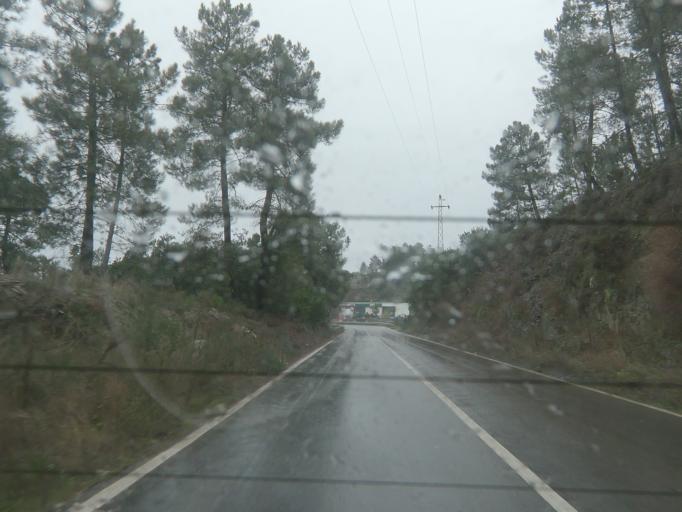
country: PT
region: Vila Real
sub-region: Sabrosa
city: Vilela
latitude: 41.2336
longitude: -7.6820
